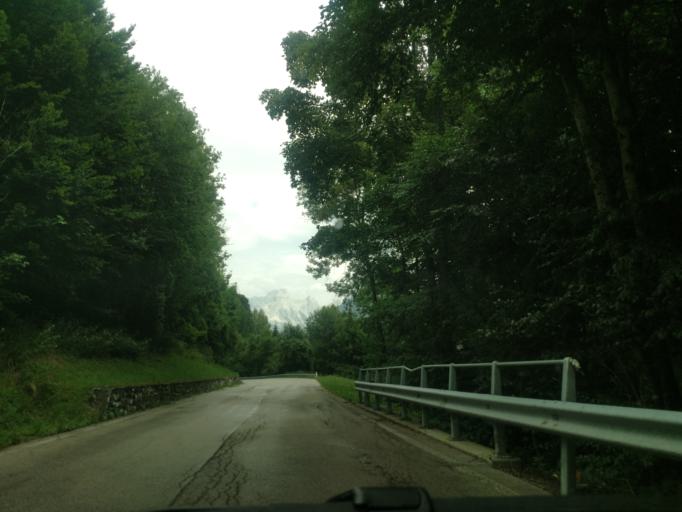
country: IT
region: Veneto
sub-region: Provincia di Belluno
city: Rivamonte Agordino
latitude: 46.2357
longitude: 12.0150
